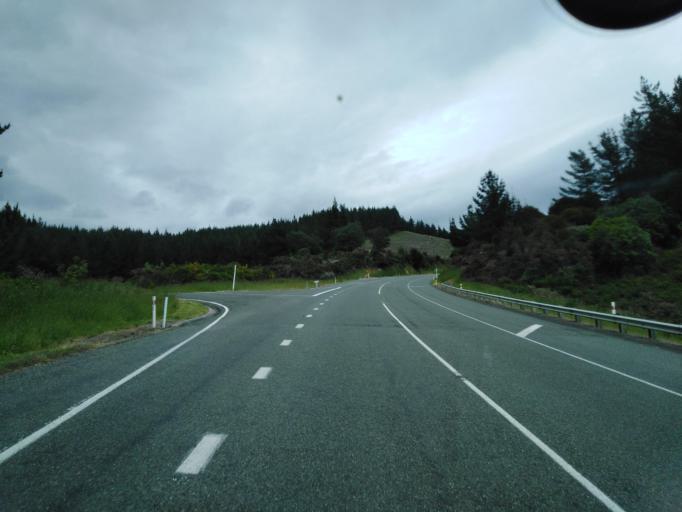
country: NZ
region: Tasman
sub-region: Tasman District
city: Wakefield
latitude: -41.4787
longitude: 172.9284
